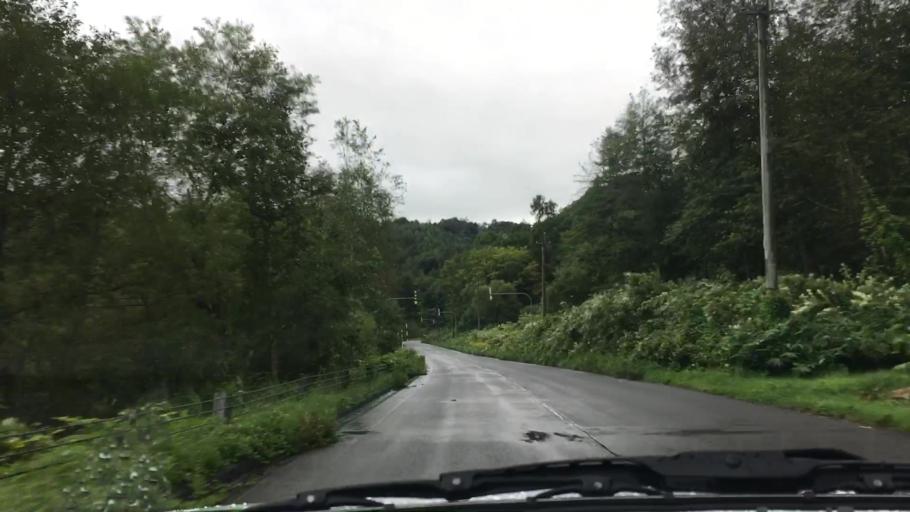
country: JP
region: Hokkaido
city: Niseko Town
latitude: 42.6657
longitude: 140.7776
